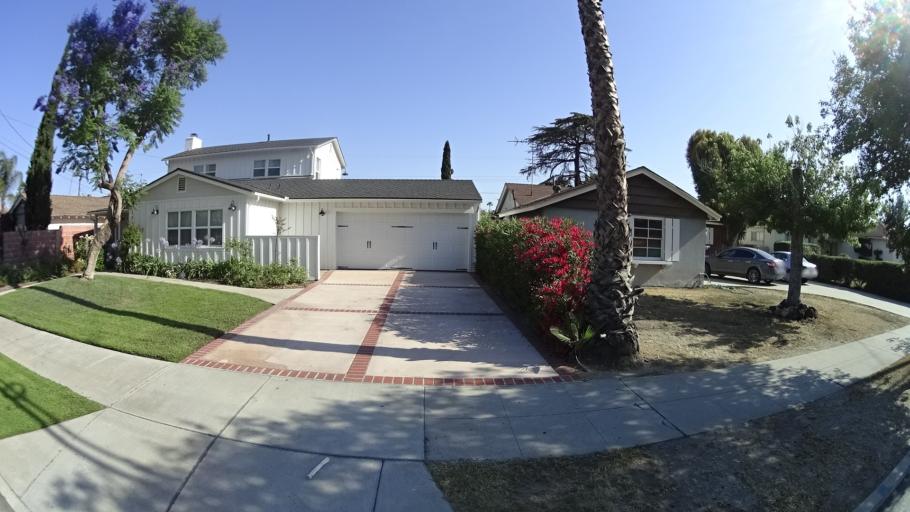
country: US
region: California
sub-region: Los Angeles County
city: Van Nuys
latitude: 34.2198
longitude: -118.4196
